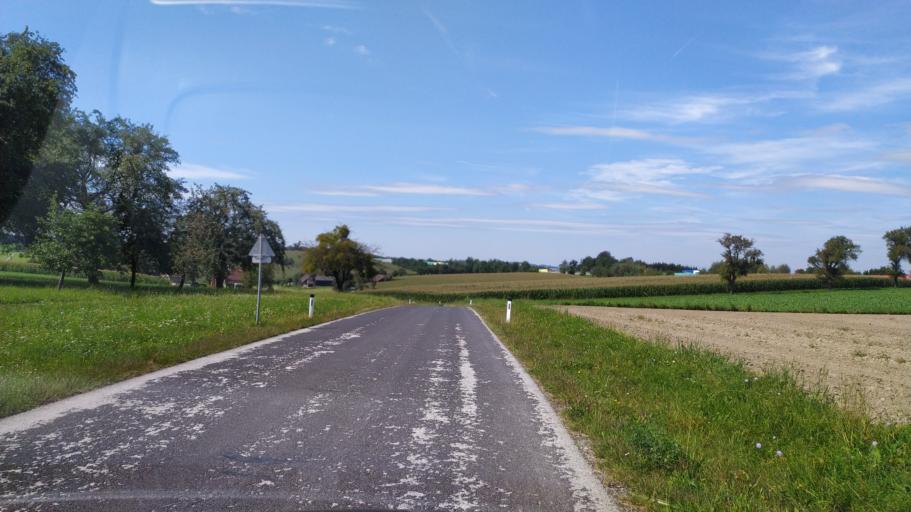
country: AT
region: Lower Austria
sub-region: Politischer Bezirk Amstetten
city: Strengberg
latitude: 48.1148
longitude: 14.6569
